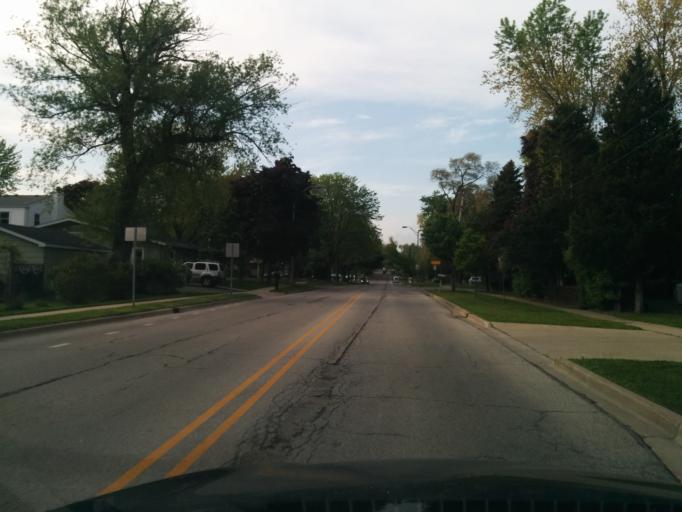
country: US
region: Illinois
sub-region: DuPage County
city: Lombard
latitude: 41.8908
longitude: -88.0084
